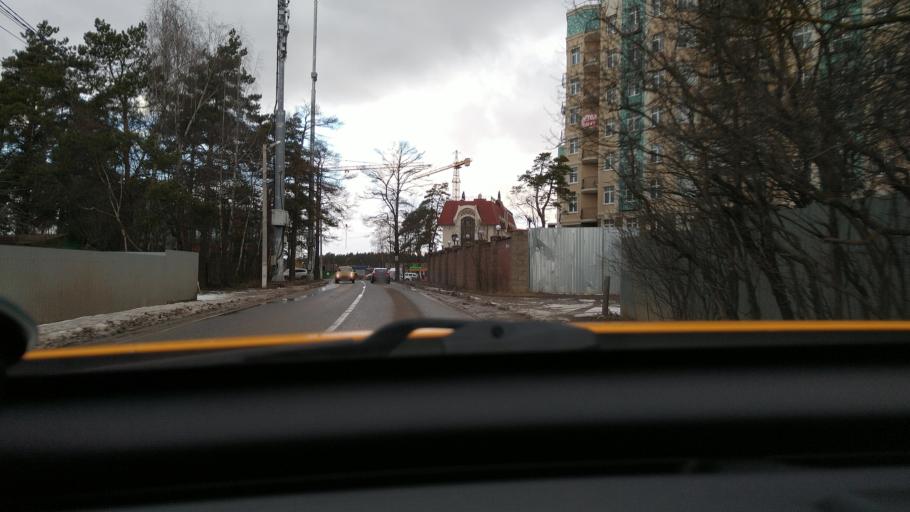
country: RU
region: Moskovskaya
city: Petrovo-Dal'neye
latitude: 55.7720
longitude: 37.2180
